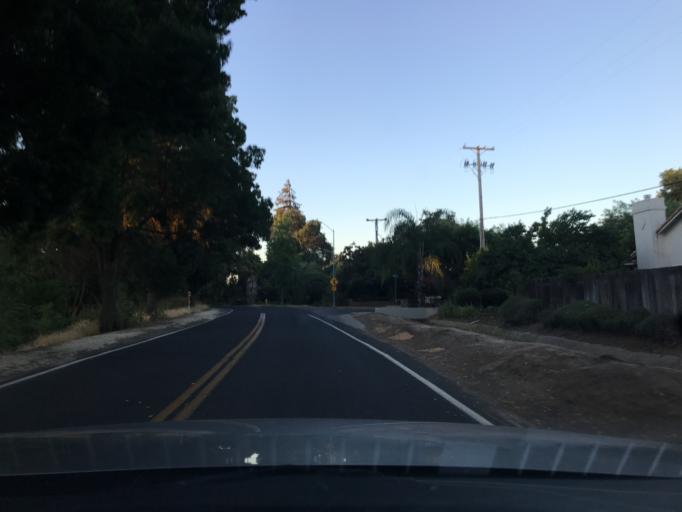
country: US
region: California
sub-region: Merced County
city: Merced
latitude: 37.3113
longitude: -120.4989
